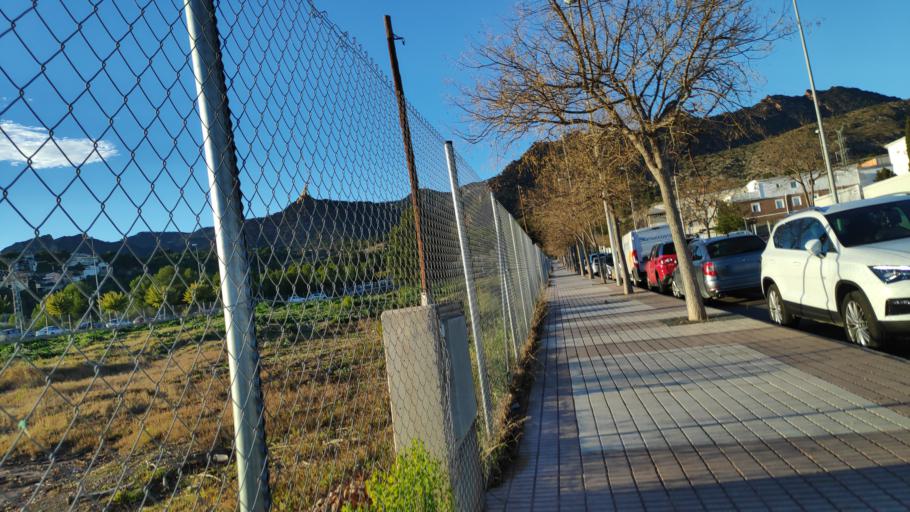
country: ES
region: Valencia
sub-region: Provincia de Castello
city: Benicassim
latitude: 40.0565
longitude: 0.0608
